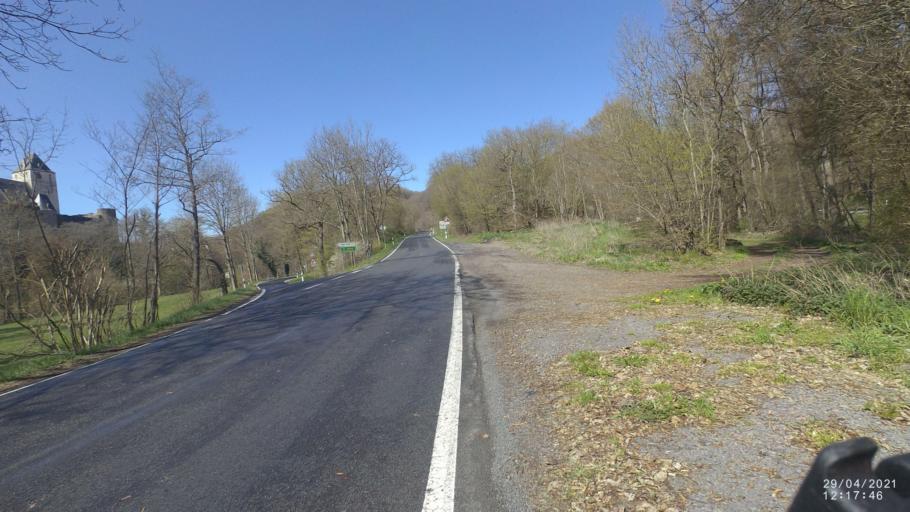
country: DE
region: Rheinland-Pfalz
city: Sankt Johann
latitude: 50.3534
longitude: 7.1821
